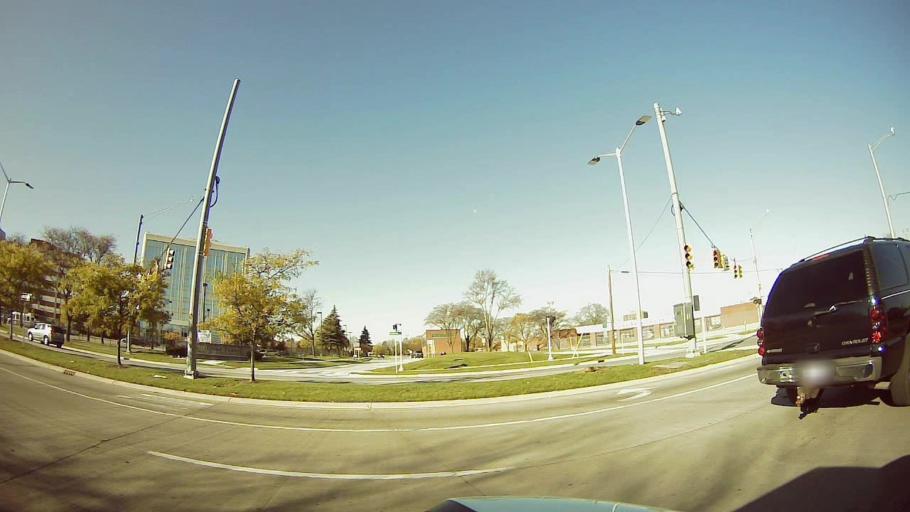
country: US
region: Michigan
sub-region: Oakland County
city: Oak Park
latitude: 42.4478
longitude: -83.2005
